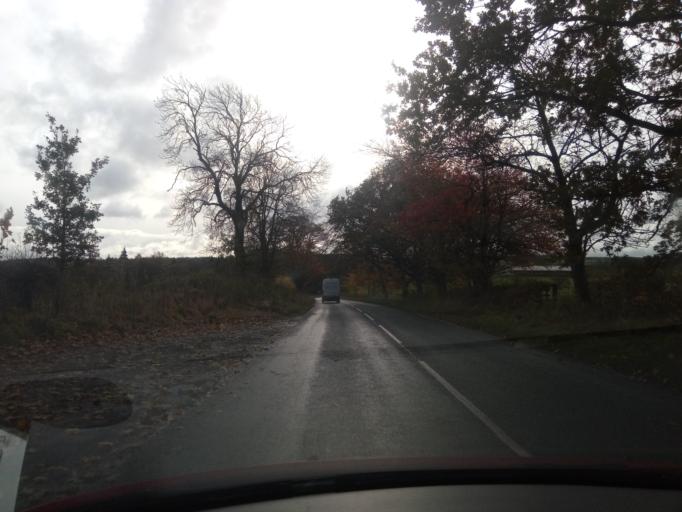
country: GB
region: England
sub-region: Northumberland
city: Birtley
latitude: 55.0668
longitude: -2.1918
